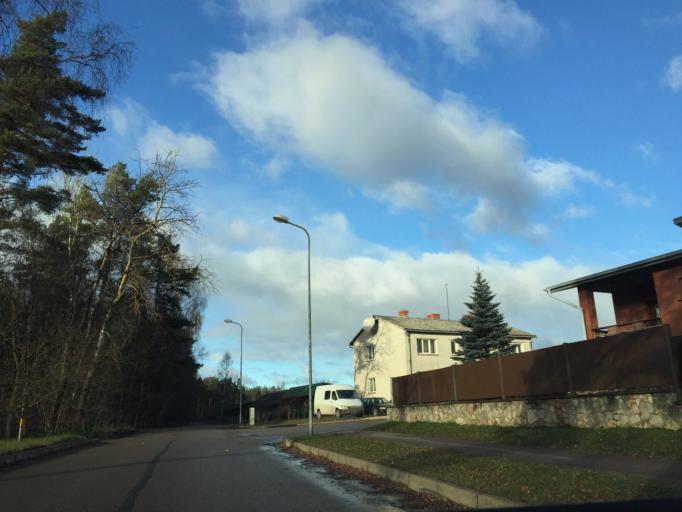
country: LV
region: Valmieras Rajons
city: Valmiera
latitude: 57.5305
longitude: 25.3841
